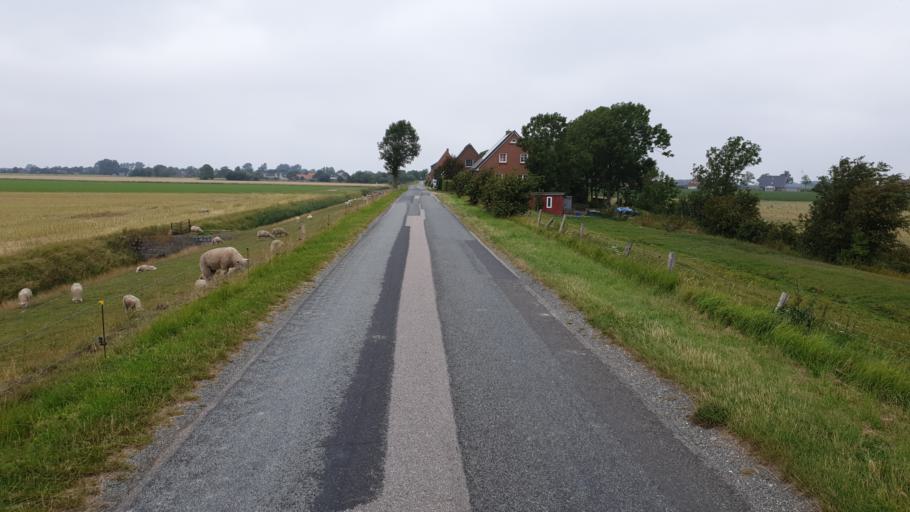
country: DE
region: Schleswig-Holstein
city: Elisabeth-Sophien-Koog
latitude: 54.4839
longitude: 8.8905
